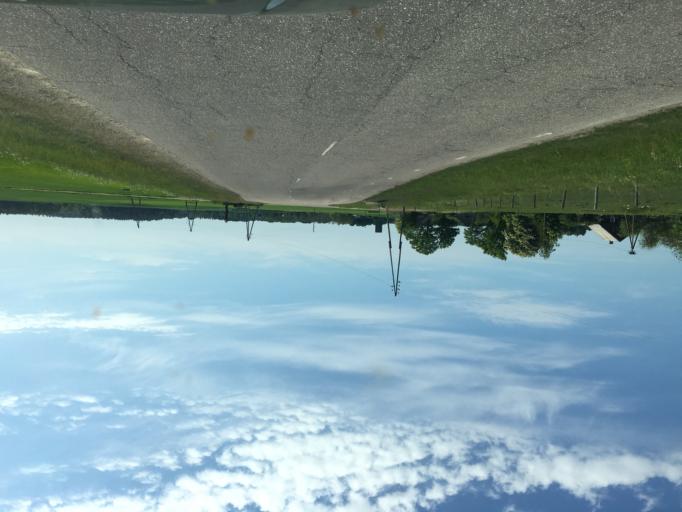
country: LV
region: Talsu Rajons
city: Valdemarpils
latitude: 57.3772
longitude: 22.5183
